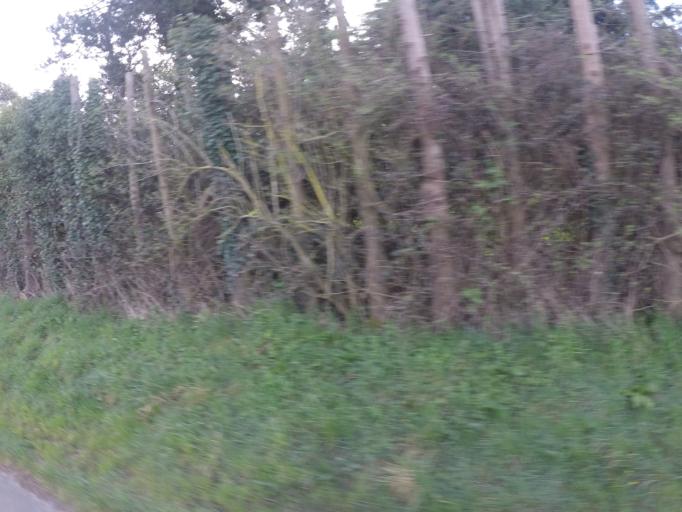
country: FR
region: Brittany
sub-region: Departement des Cotes-d'Armor
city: Lanvollon
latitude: 48.6266
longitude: -2.9884
